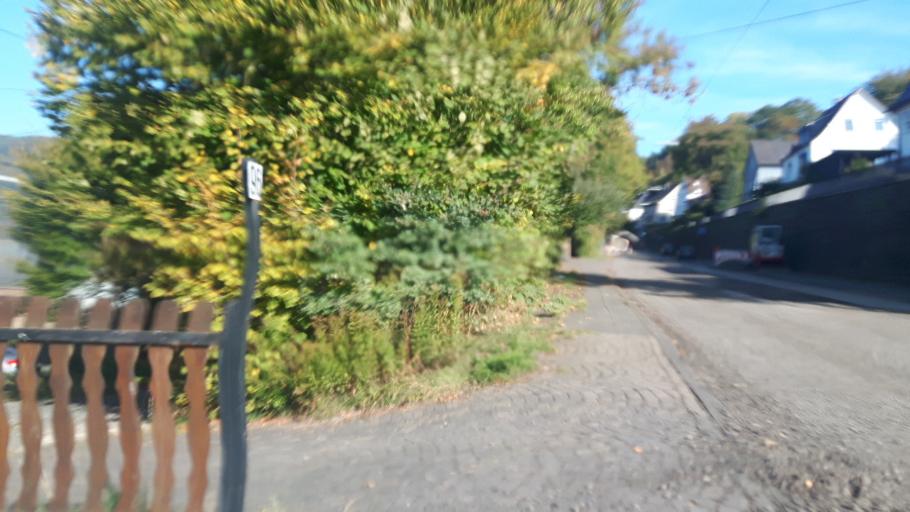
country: DE
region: North Rhine-Westphalia
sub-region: Regierungsbezirk Arnsberg
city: Siegen
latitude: 50.9064
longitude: 8.0380
